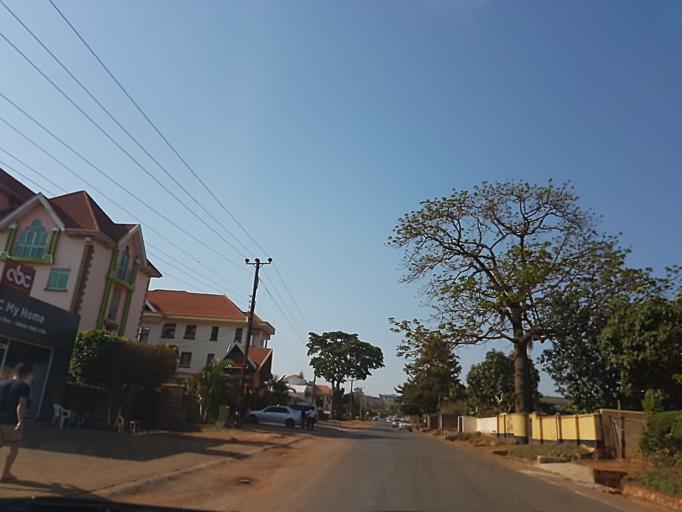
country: UG
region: Central Region
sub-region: Wakiso District
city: Kireka
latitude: 0.3466
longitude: 32.6174
